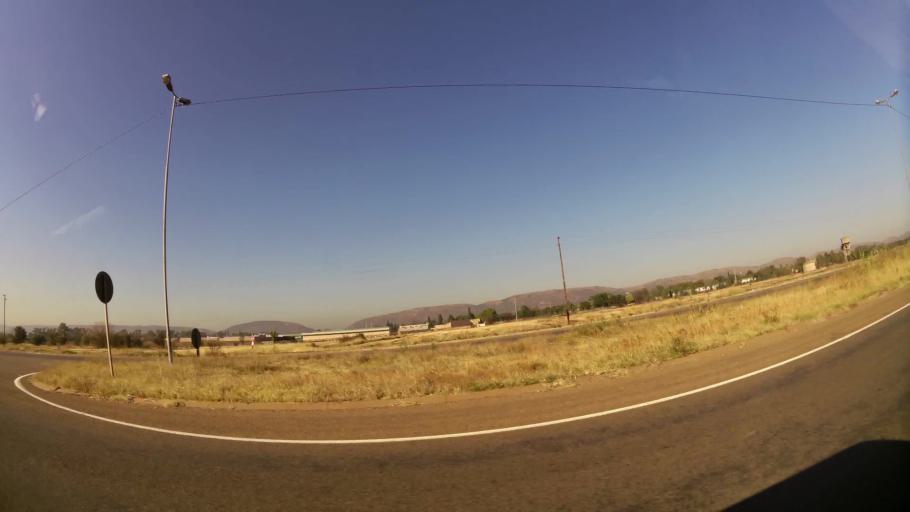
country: ZA
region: Gauteng
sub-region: City of Tshwane Metropolitan Municipality
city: Pretoria
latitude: -25.6567
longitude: 28.1791
